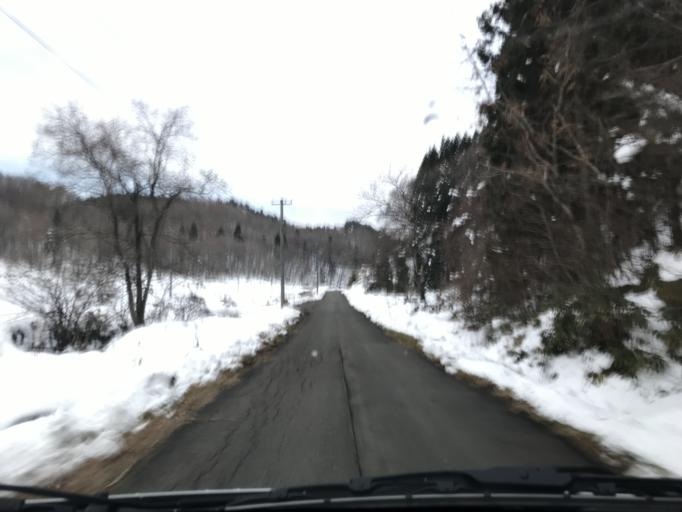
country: JP
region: Iwate
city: Mizusawa
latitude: 39.0424
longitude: 141.0111
